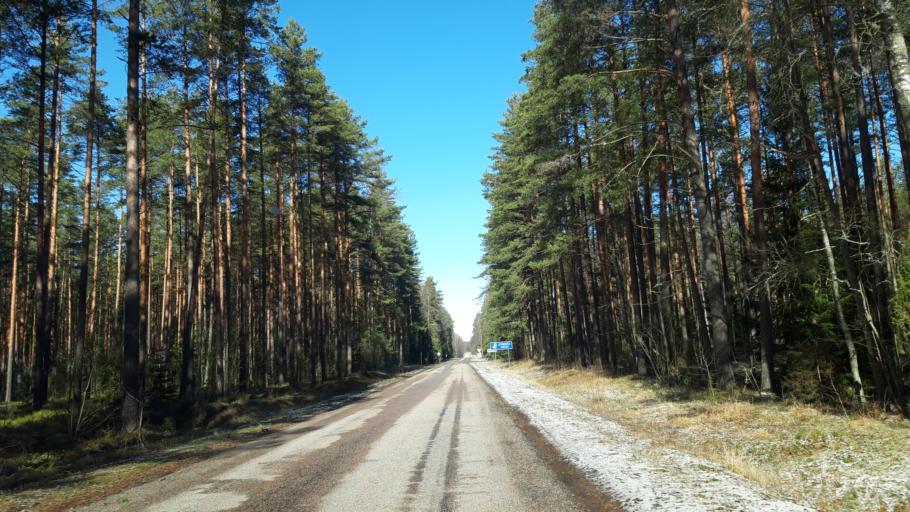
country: LV
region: Strenci
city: Strenci
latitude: 57.5985
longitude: 25.7175
